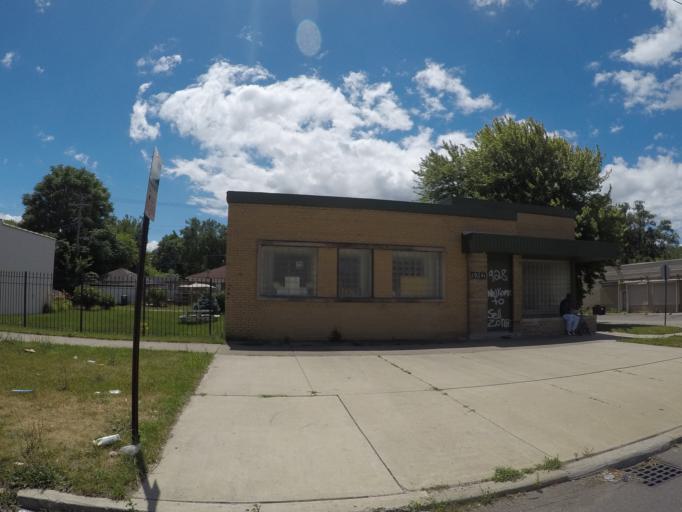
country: US
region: Michigan
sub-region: Oakland County
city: Southfield
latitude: 42.4296
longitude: -83.2364
